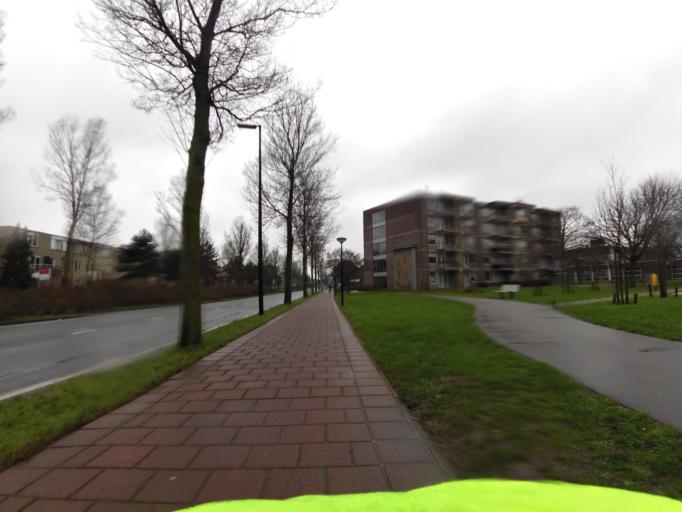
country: NL
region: South Holland
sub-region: Gemeente Maassluis
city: Maassluis
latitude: 51.9288
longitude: 4.2438
